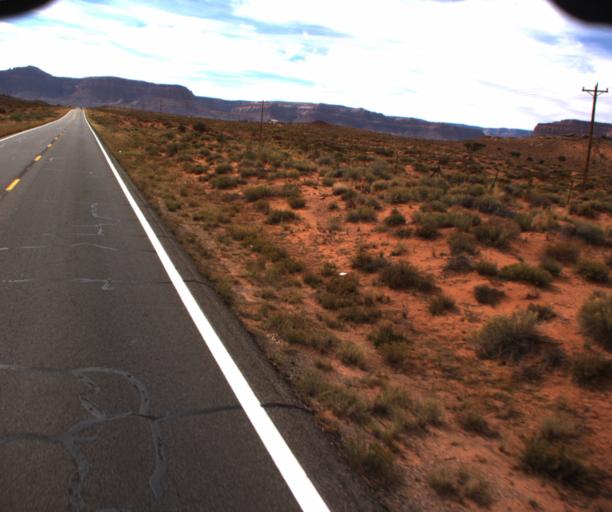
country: US
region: Arizona
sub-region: Navajo County
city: Kayenta
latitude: 36.8989
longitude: -110.2415
